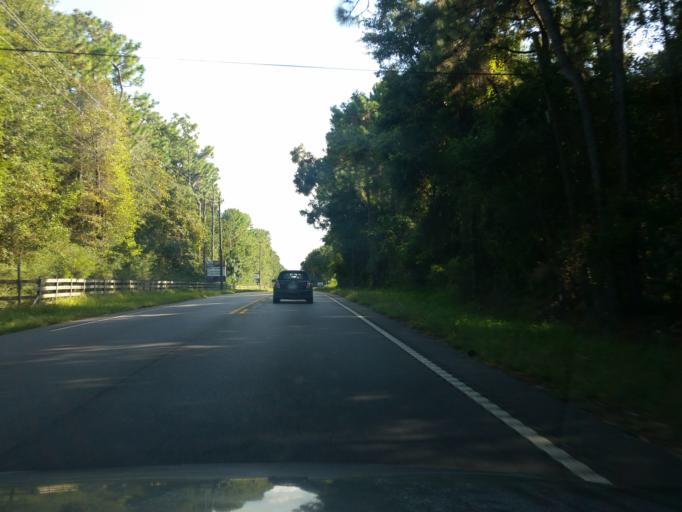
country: US
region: Alabama
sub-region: Mobile County
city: Theodore
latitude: 30.4945
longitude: -88.1116
